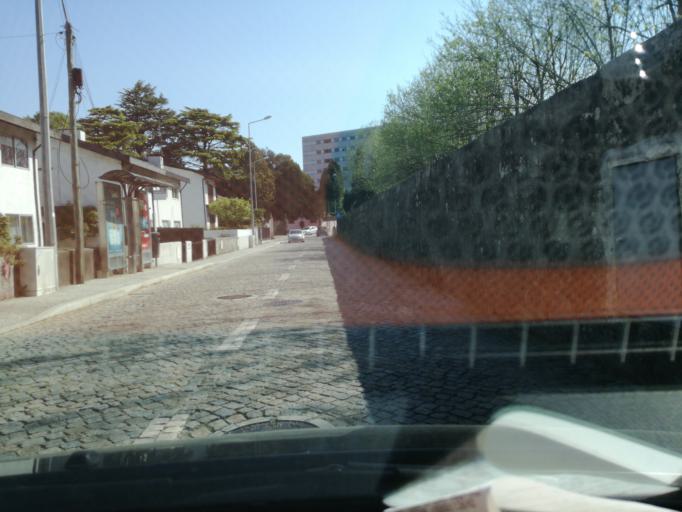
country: PT
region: Porto
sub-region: Maia
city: Maia
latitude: 41.2367
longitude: -8.6299
